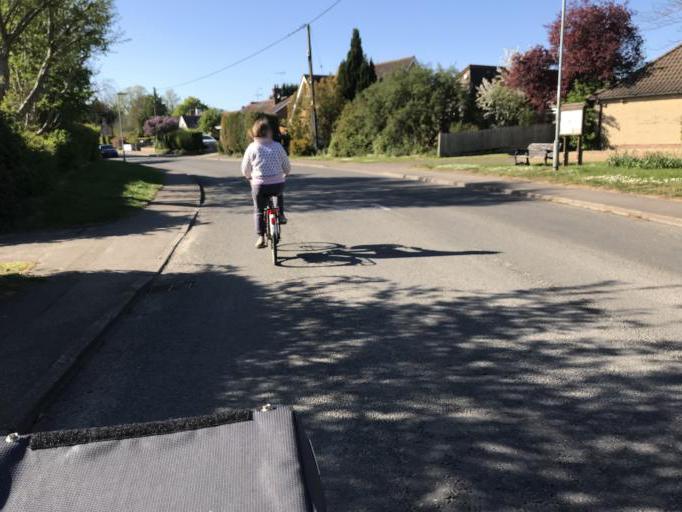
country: GB
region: England
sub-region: Cambridgeshire
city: Fulbourn
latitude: 52.2020
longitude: 0.1928
